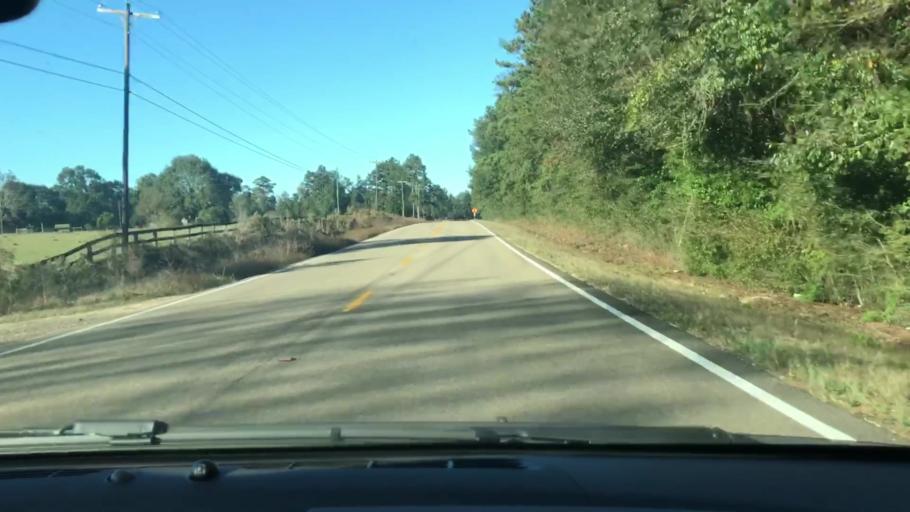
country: US
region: Louisiana
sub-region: Saint Tammany Parish
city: Abita Springs
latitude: 30.6341
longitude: -90.0159
